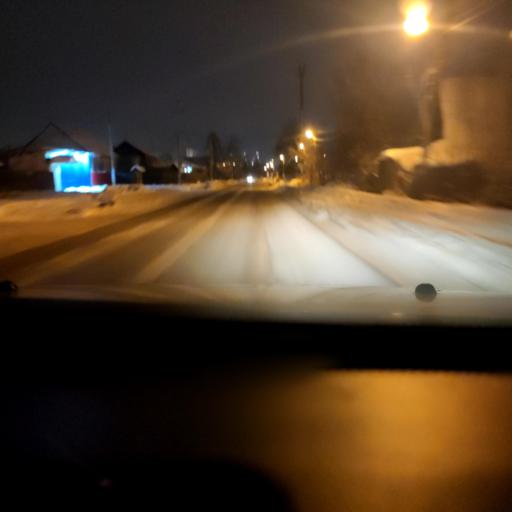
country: RU
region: Perm
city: Kondratovo
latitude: 58.0491
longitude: 56.0303
